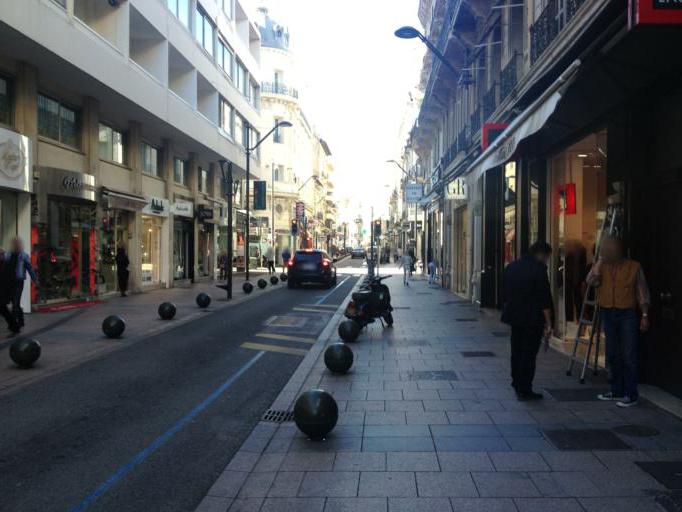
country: FR
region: Provence-Alpes-Cote d'Azur
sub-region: Departement des Alpes-Maritimes
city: Cannes
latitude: 43.5522
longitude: 7.0270
